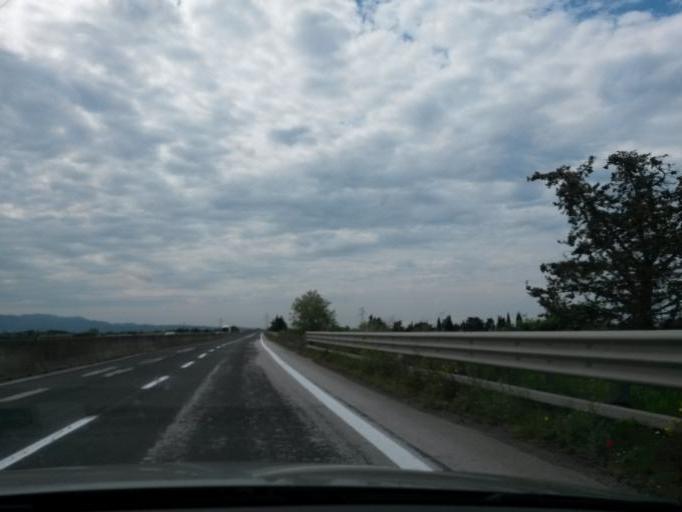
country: IT
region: Tuscany
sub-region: Provincia di Livorno
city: La California
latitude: 43.2400
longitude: 10.5560
